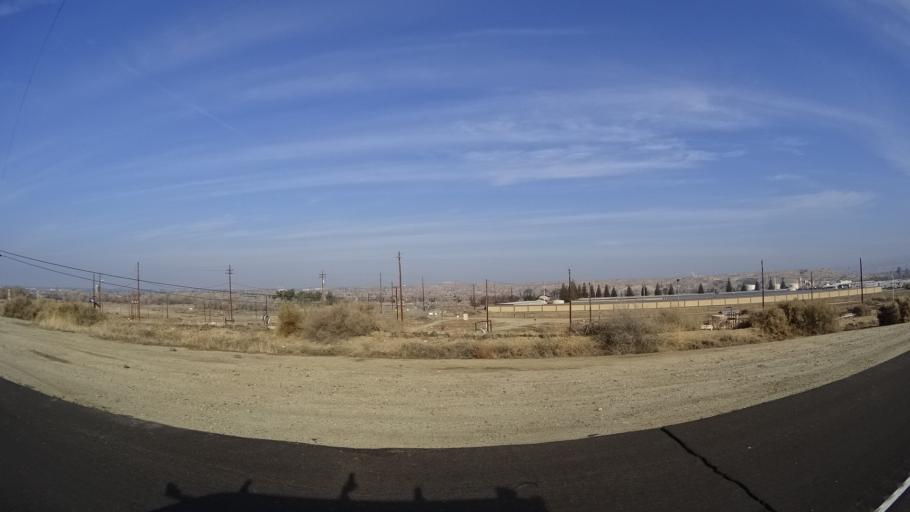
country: US
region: California
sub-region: Kern County
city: Oildale
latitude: 35.4164
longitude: -118.9668
